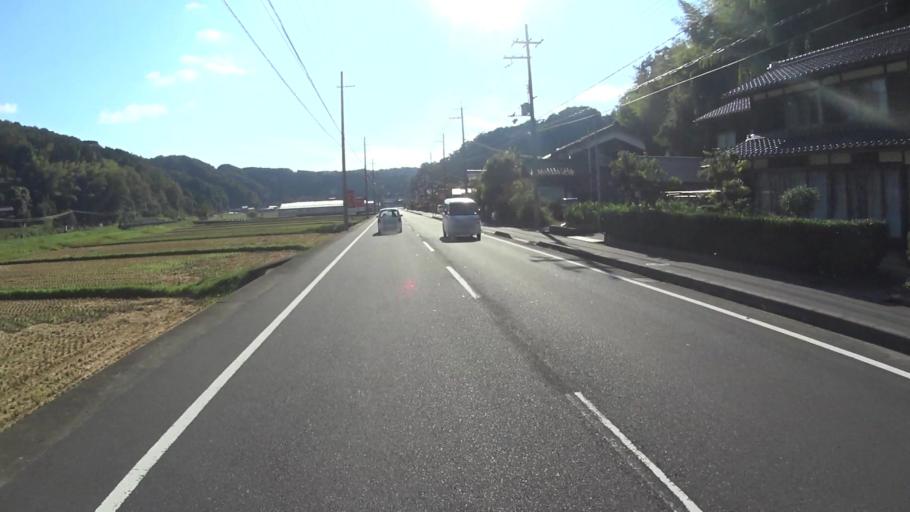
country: JP
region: Hyogo
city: Toyooka
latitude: 35.6533
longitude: 134.9810
